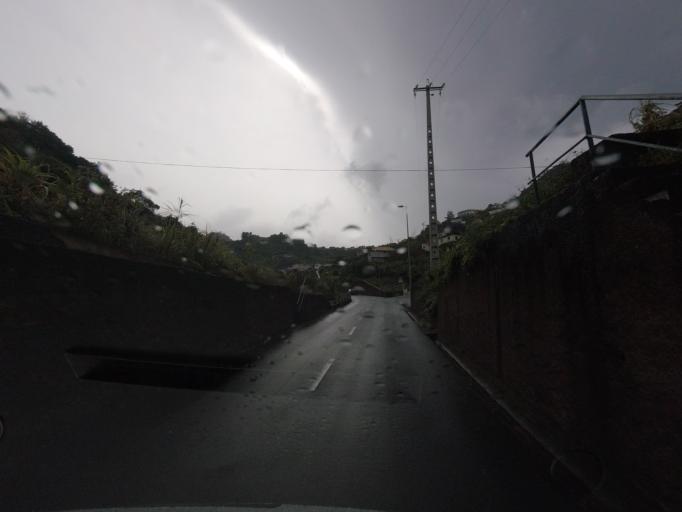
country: PT
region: Madeira
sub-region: Santana
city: Santana
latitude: 32.7712
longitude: -16.8341
